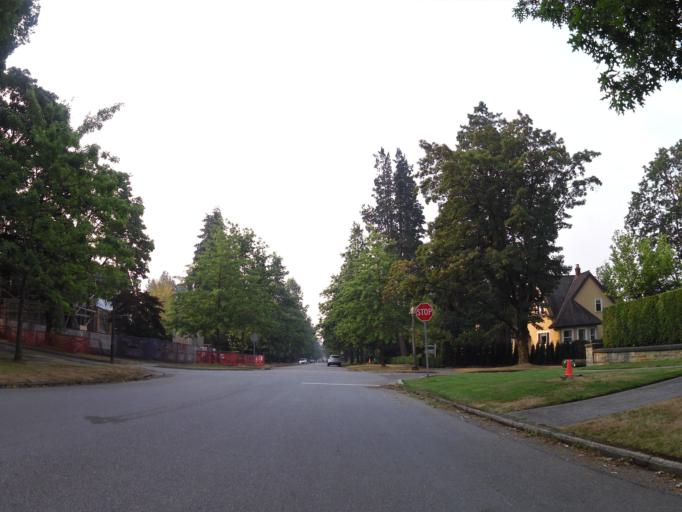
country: CA
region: British Columbia
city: Vancouver
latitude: 49.2329
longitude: -123.1478
